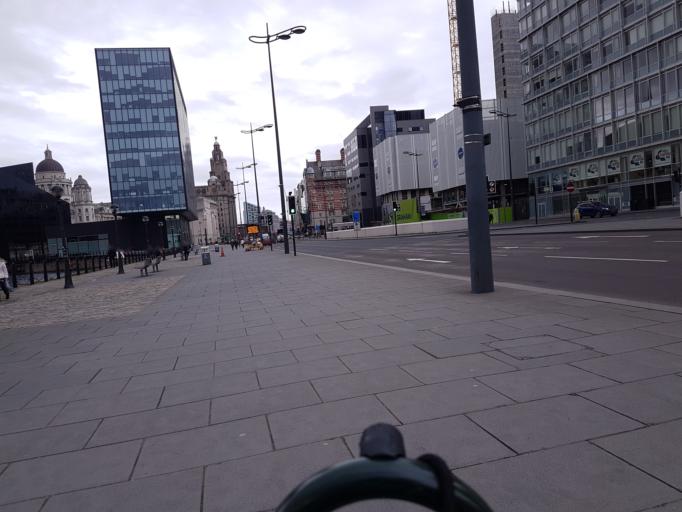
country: GB
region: England
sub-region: Liverpool
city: Liverpool
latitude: 53.4025
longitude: -2.9905
